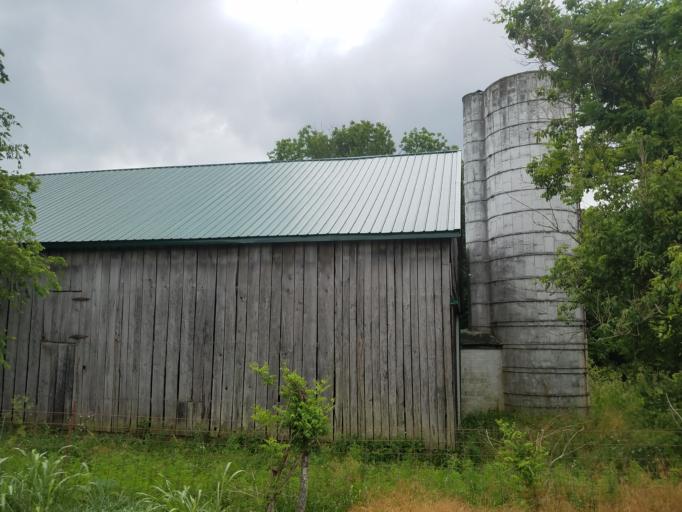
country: US
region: Kentucky
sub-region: Washington County
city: Springfield
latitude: 37.7599
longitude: -85.2462
